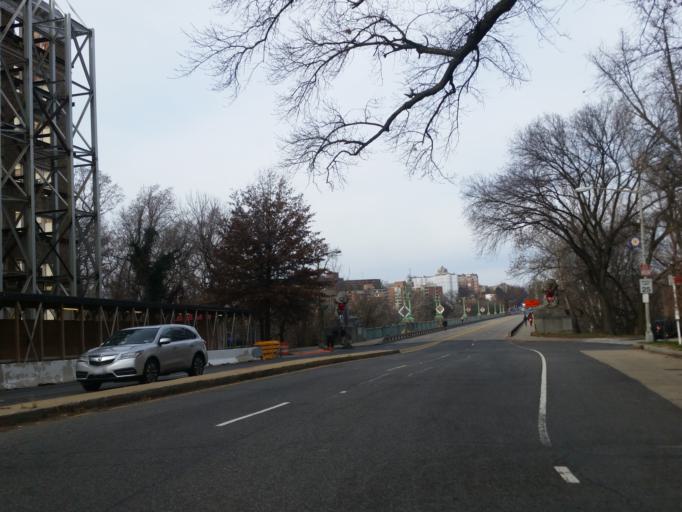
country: US
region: Washington, D.C.
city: Washington, D.C.
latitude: 38.9189
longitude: -77.0487
